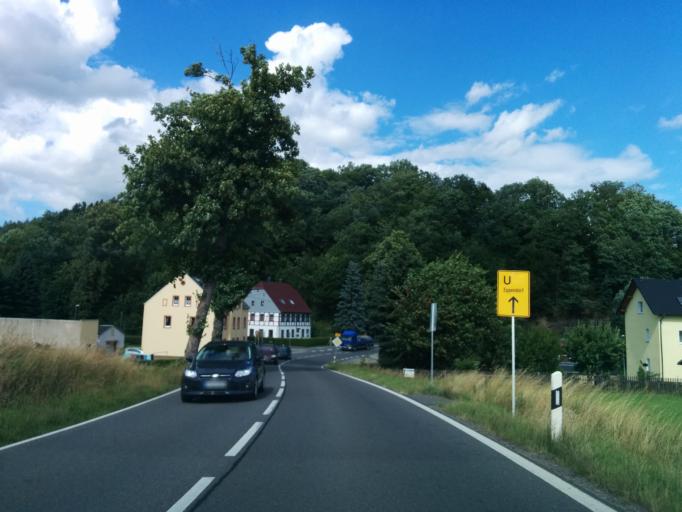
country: DE
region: Saxony
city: Falkenau
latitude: 50.8572
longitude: 13.1055
